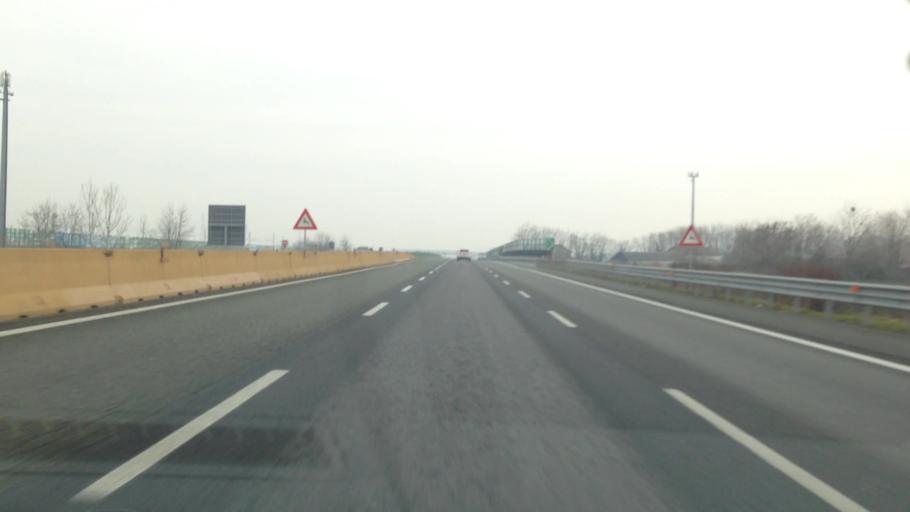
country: IT
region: Piedmont
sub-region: Provincia di Vercelli
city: Alice Castello
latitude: 45.3635
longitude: 8.1184
